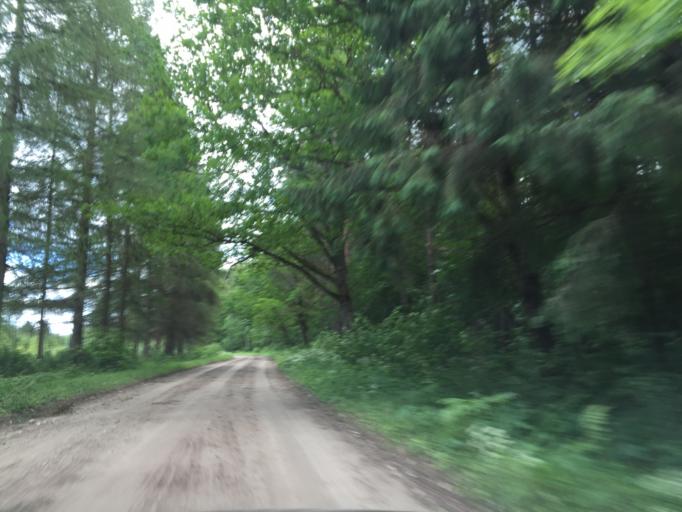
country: LV
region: Lecava
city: Iecava
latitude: 56.5904
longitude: 24.2267
